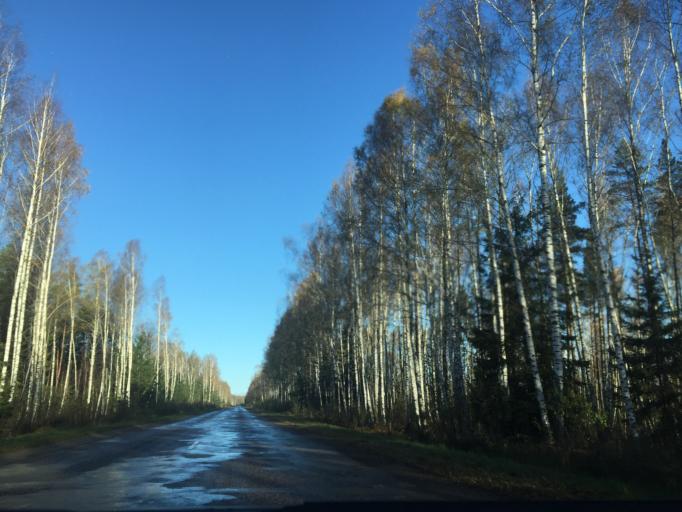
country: LV
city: Tireli
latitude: 56.9048
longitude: 23.5289
